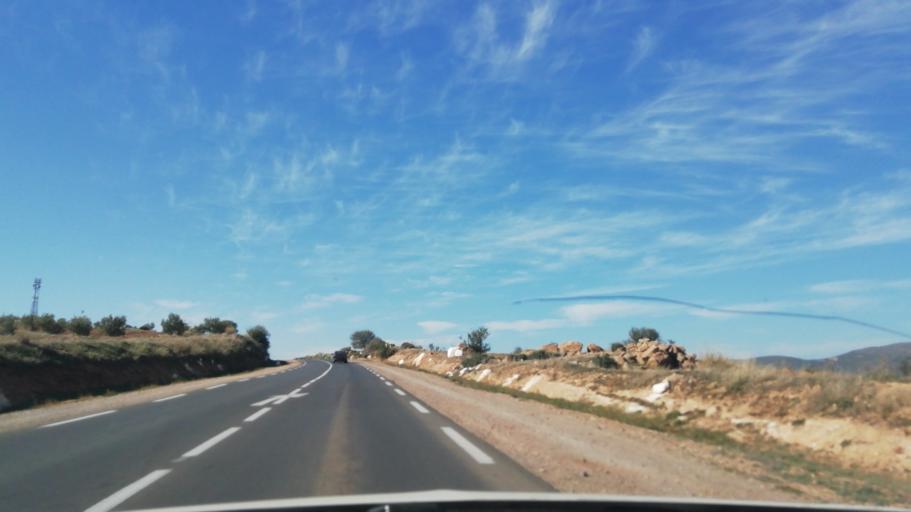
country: DZ
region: Tlemcen
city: Ouled Mimoun
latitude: 34.8769
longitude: -1.1140
